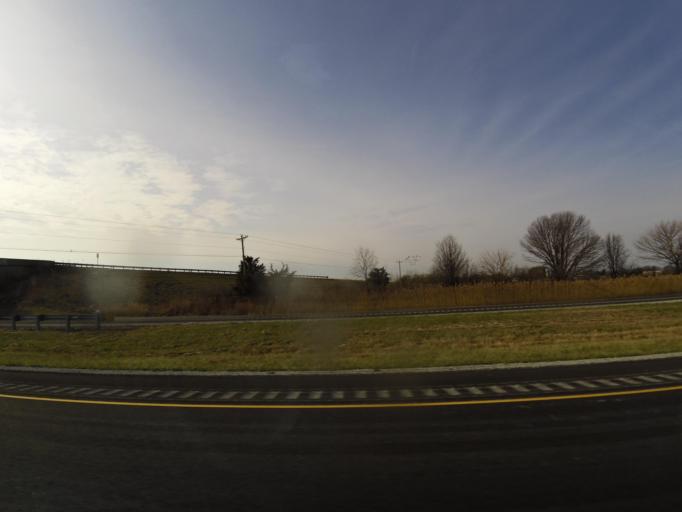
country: US
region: Illinois
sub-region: Macon County
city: Decatur
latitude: 39.7781
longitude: -88.9692
